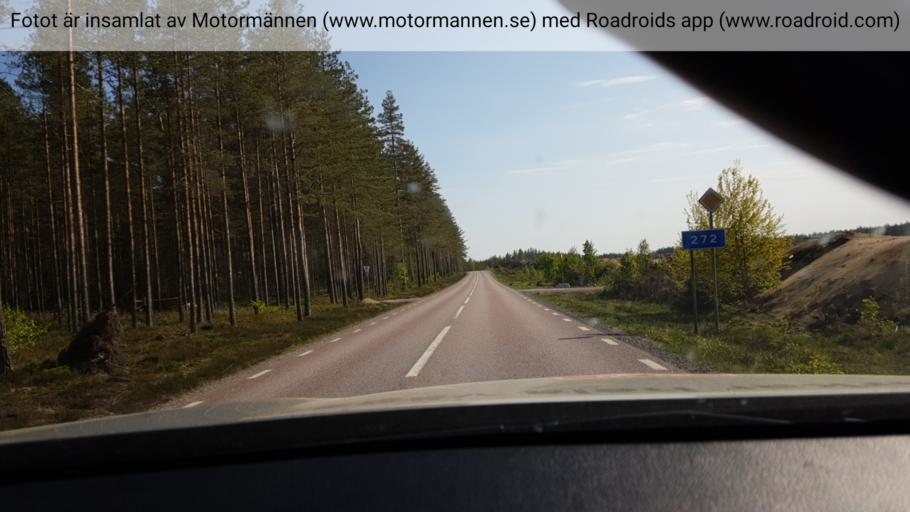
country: SE
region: Gaevleborg
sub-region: Sandvikens Kommun
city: Arsunda
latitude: 60.4752
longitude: 16.7118
